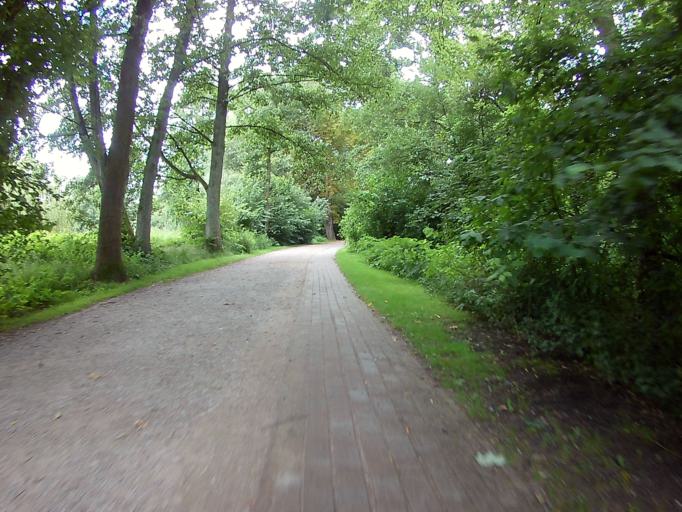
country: DE
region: Hamburg
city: Harburg
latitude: 53.4420
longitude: 9.9775
